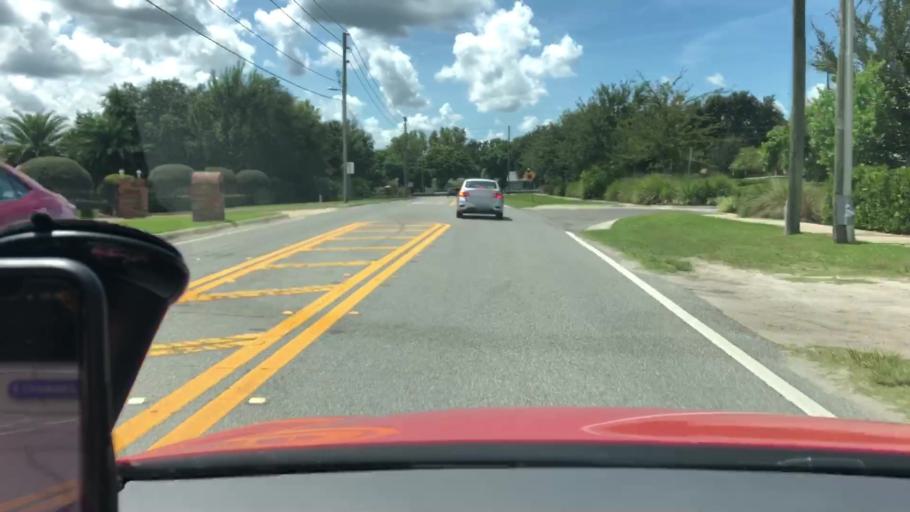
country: US
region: Florida
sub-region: Lake County
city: Mount Dora
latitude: 28.8344
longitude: -81.6545
